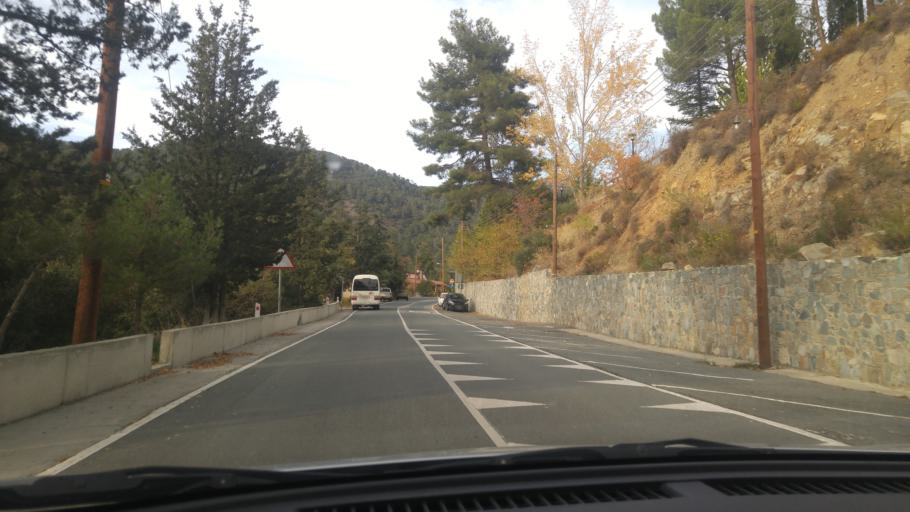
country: CY
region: Lefkosia
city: Kakopetria
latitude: 34.8955
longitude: 32.8370
